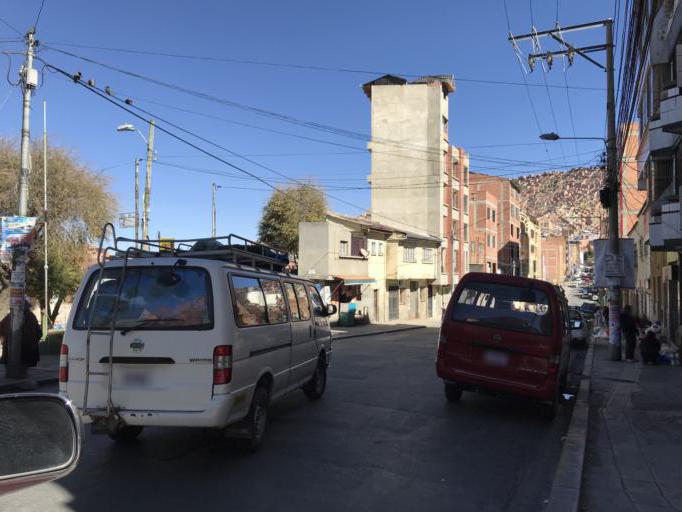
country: BO
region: La Paz
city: La Paz
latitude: -16.4916
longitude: -68.1510
